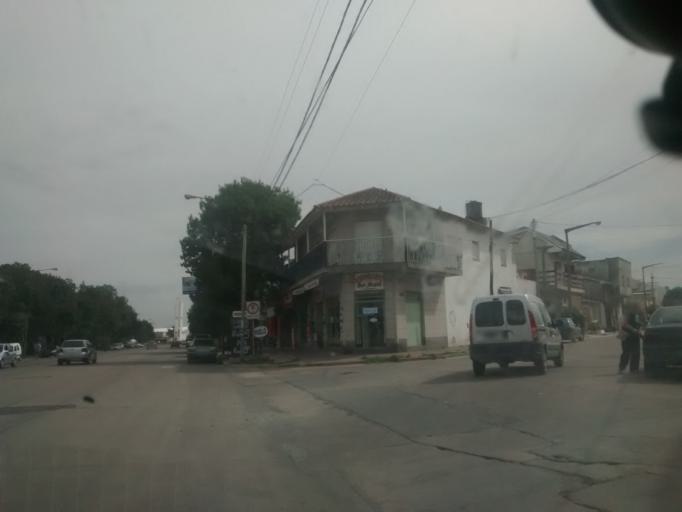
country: AR
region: Buenos Aires
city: Necochea
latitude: -38.5652
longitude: -58.7295
